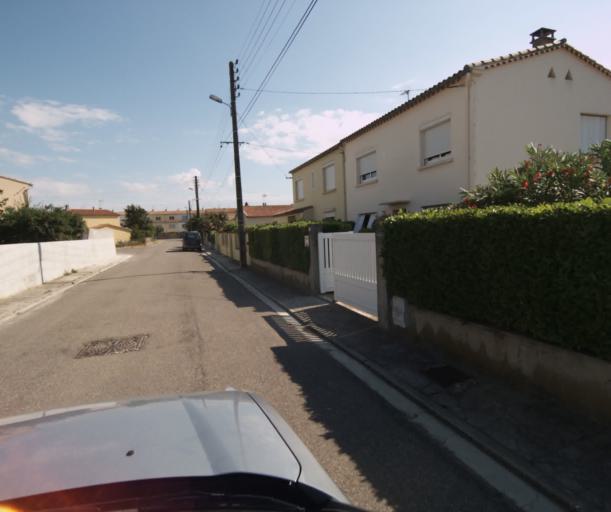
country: FR
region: Languedoc-Roussillon
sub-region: Departement de l'Aude
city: Limoux
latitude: 43.0657
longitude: 2.2195
